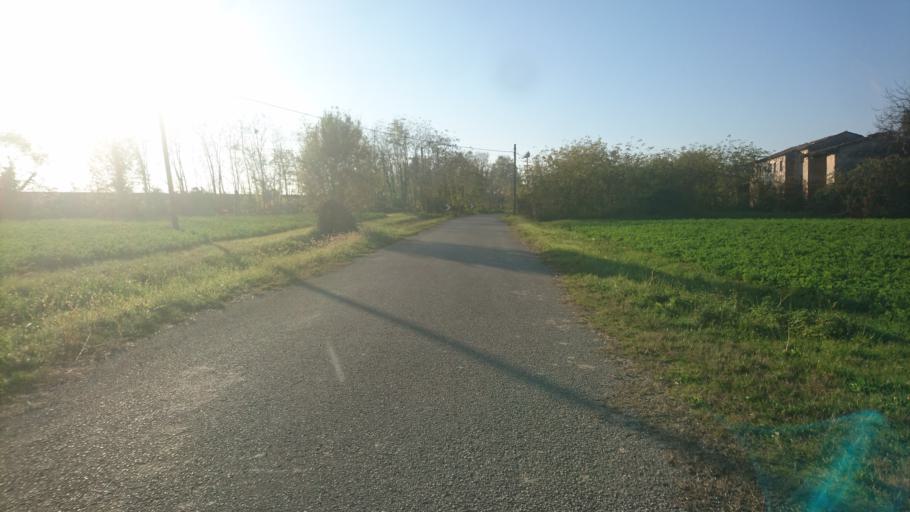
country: IT
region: Veneto
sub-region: Provincia di Padova
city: Villaguattera
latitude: 45.4401
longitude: 11.8263
